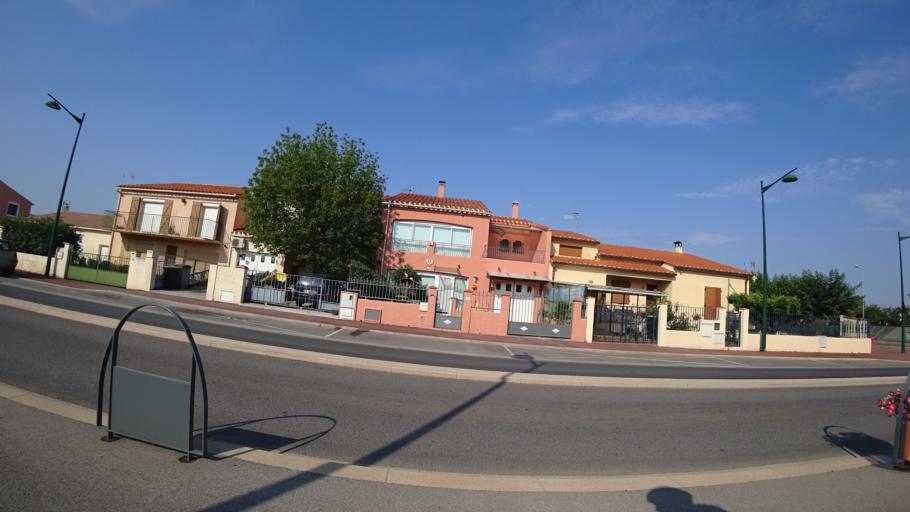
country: FR
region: Languedoc-Roussillon
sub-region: Departement des Pyrenees-Orientales
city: Bompas
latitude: 42.7254
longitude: 2.9366
